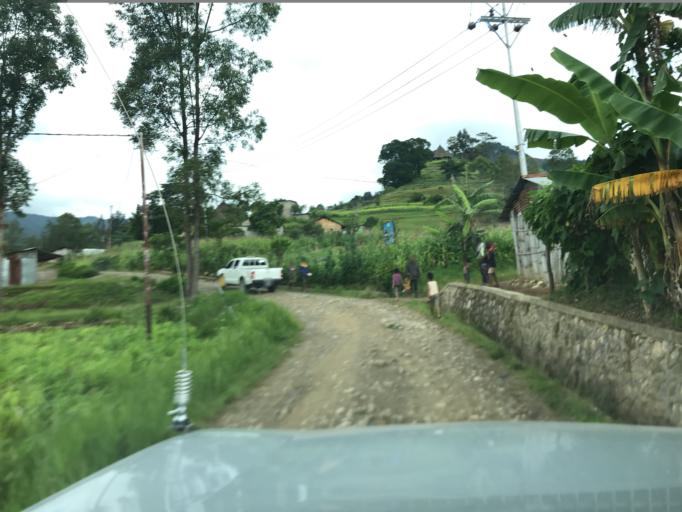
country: TL
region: Aileu
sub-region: Aileu Villa
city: Aileu
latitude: -8.8495
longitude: 125.5893
